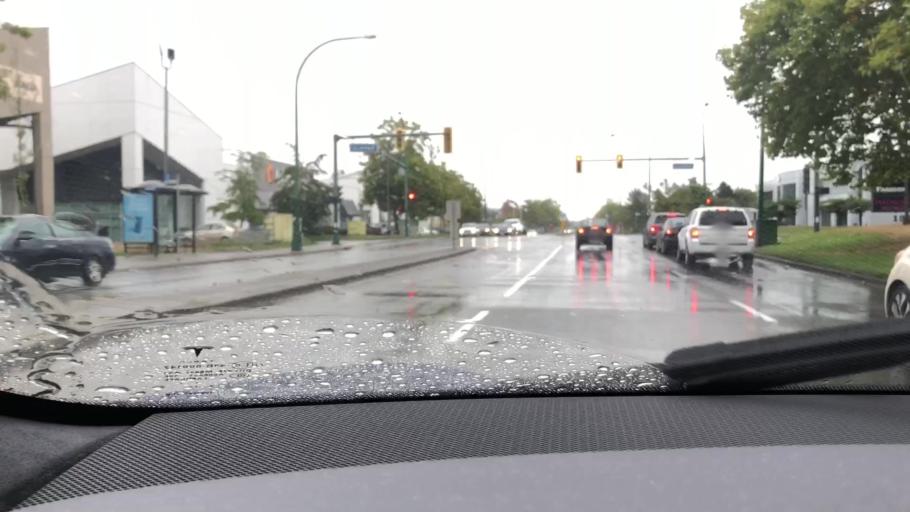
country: CA
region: British Columbia
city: Port Moody
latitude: 49.2291
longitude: -122.8535
